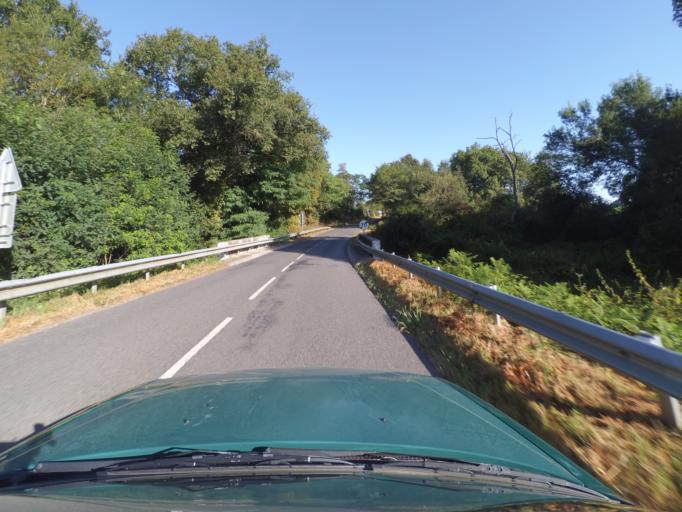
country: FR
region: Pays de la Loire
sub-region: Departement de la Loire-Atlantique
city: Les Sorinieres
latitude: 47.1189
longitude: -1.5251
